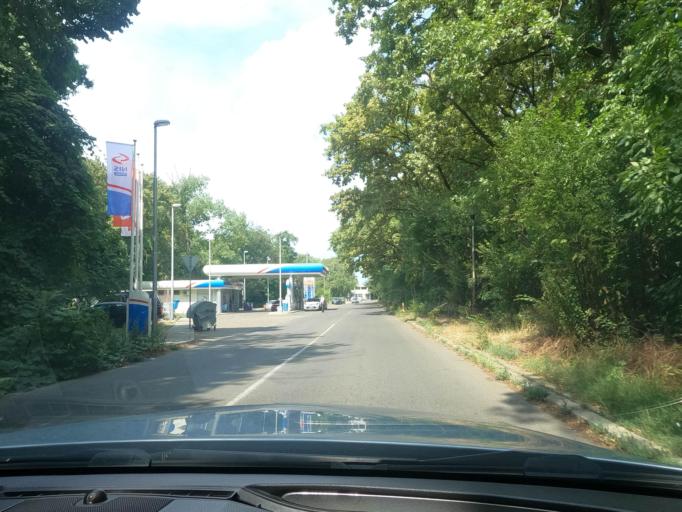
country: RS
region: Central Serbia
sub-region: Belgrade
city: Zemun
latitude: 44.8263
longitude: 20.3874
